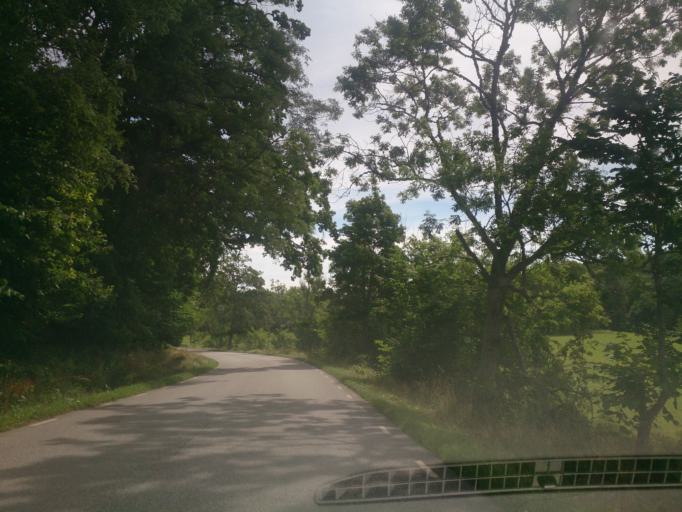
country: SE
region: OEstergoetland
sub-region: Atvidabergs Kommun
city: Atvidaberg
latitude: 58.2778
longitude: 16.1857
